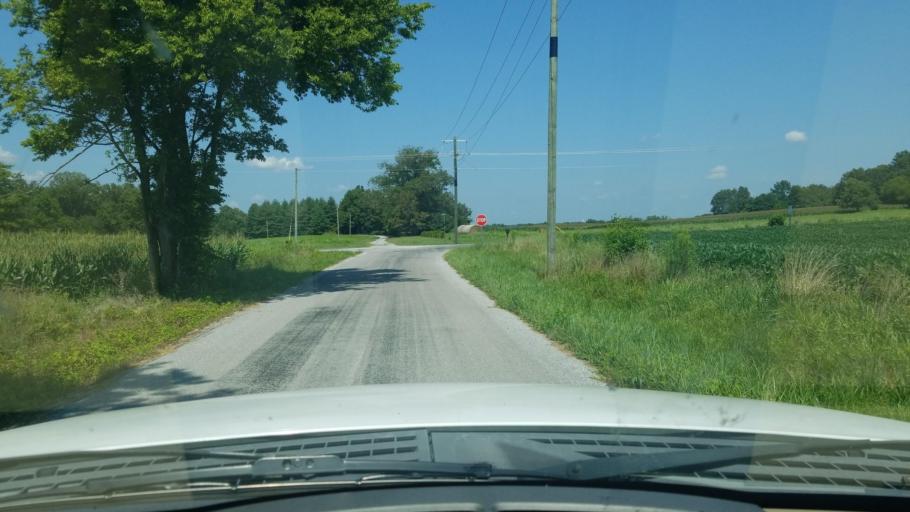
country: US
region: Illinois
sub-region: Saline County
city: Harrisburg
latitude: 37.8043
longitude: -88.6240
